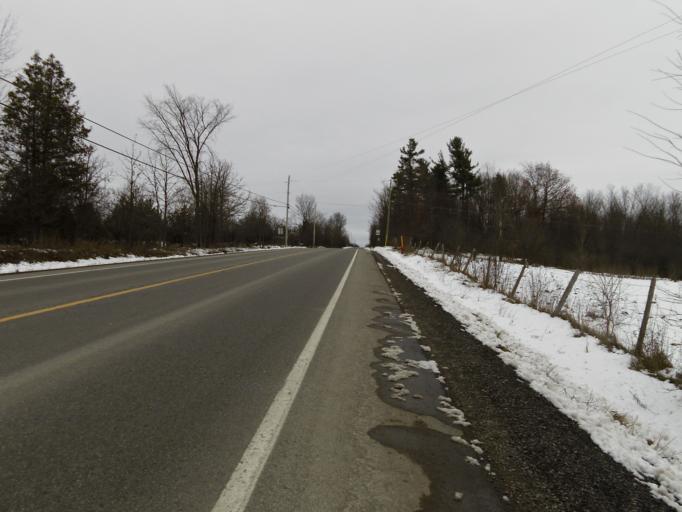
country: CA
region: Ontario
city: Carleton Place
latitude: 45.2394
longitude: -76.2060
